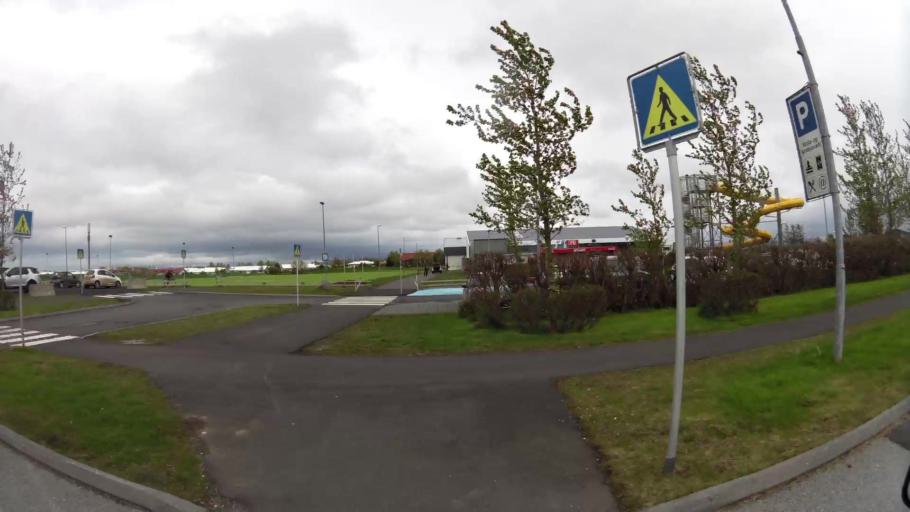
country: IS
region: Capital Region
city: Alftanes
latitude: 64.1040
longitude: -22.0208
